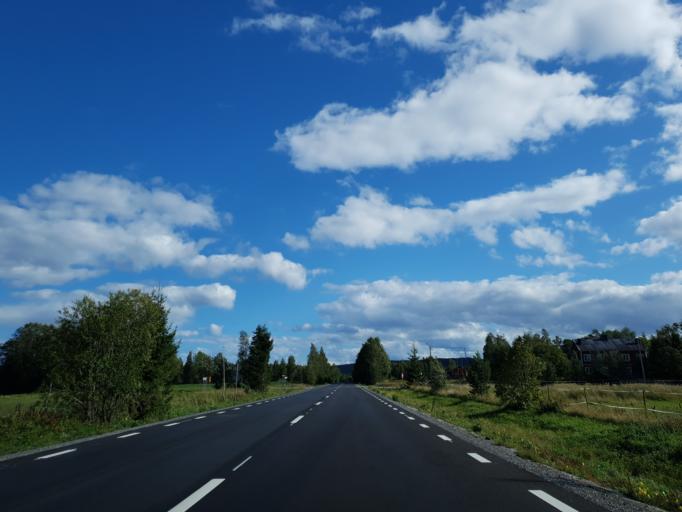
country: SE
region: Vaesternorrland
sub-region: OErnskoeldsviks Kommun
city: Kopmanholmen
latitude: 63.1790
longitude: 18.5345
